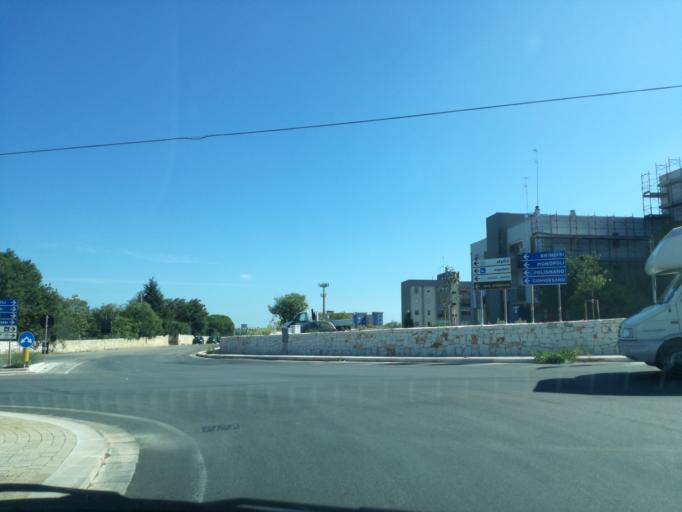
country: IT
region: Apulia
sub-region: Provincia di Bari
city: Castellana
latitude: 40.8820
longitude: 17.1498
